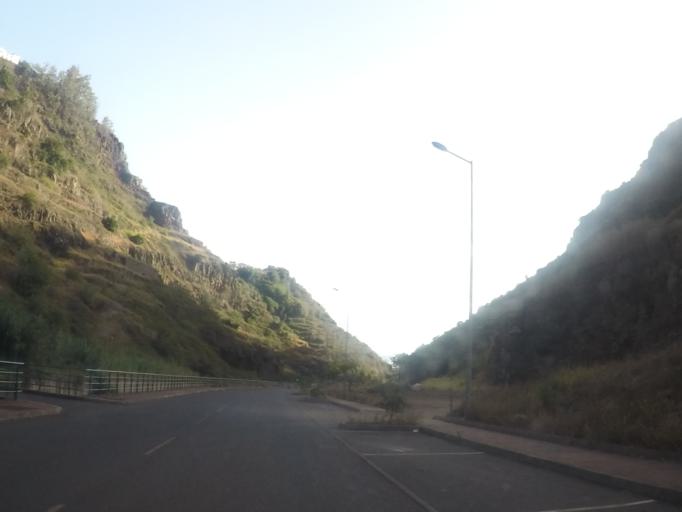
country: PT
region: Madeira
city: Ponta do Sol
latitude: 32.6930
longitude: -17.0918
